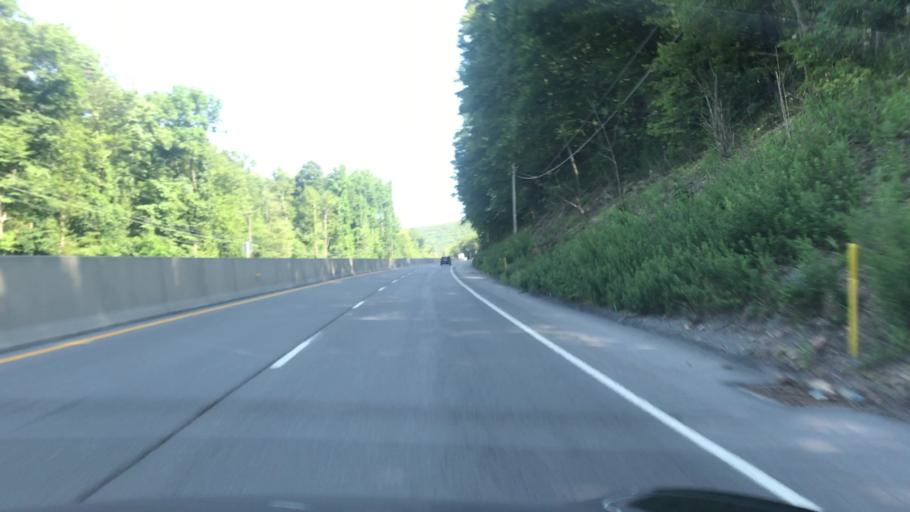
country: US
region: Pennsylvania
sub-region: Lycoming County
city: Montgomery
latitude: 41.2014
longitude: -76.9196
